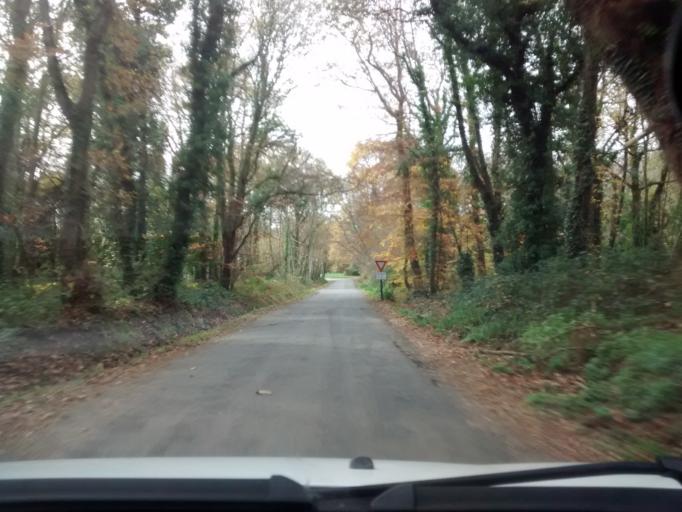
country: FR
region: Brittany
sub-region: Departement d'Ille-et-Vilaine
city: Dinard
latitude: 48.6124
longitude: -2.0752
